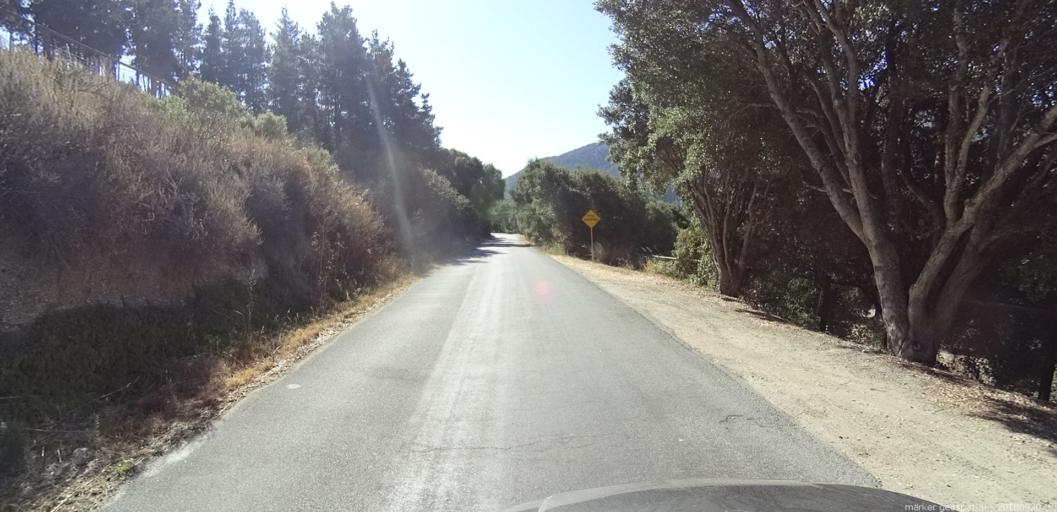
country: US
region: California
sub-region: Monterey County
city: Carmel Valley Village
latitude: 36.5229
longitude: -121.7928
